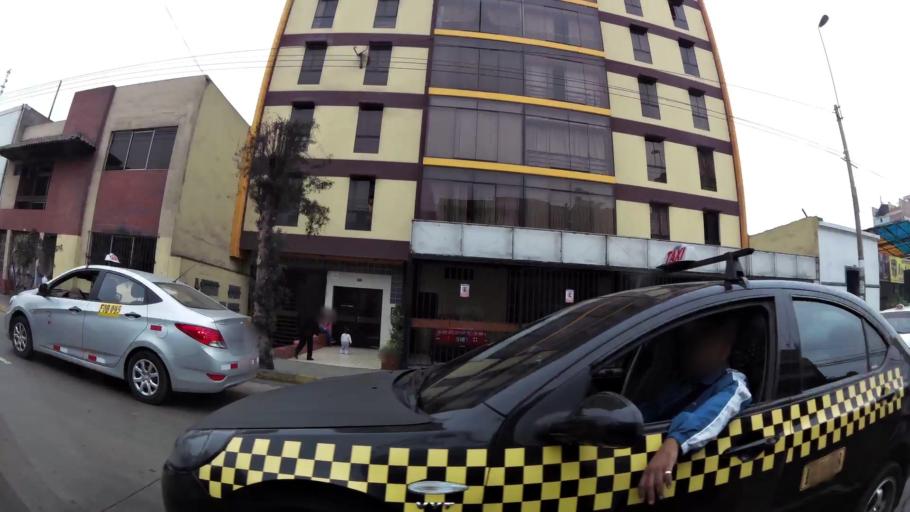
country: PE
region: Lima
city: Lima
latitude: -12.0769
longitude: -77.0344
